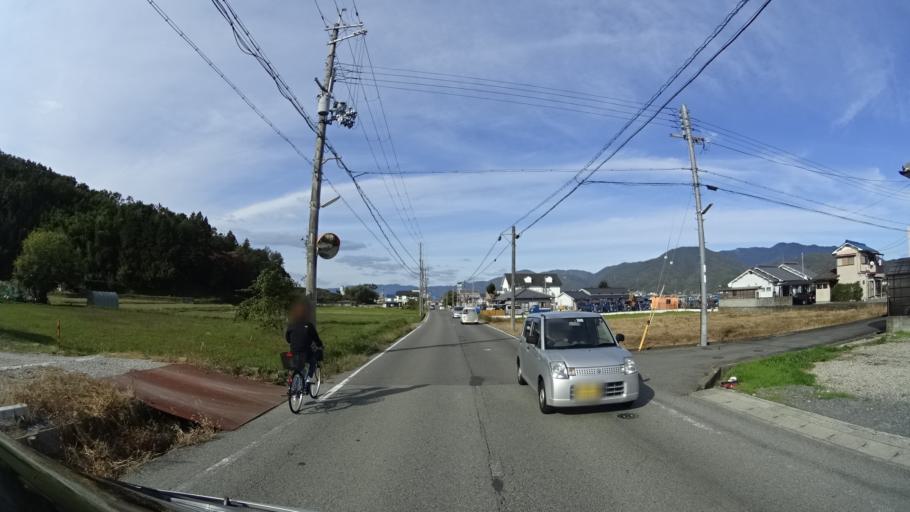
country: JP
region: Kyoto
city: Kameoka
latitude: 35.0028
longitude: 135.5781
